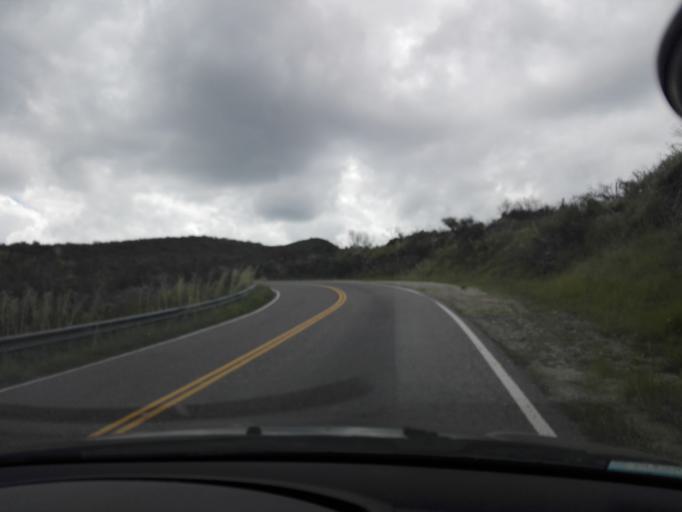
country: AR
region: Cordoba
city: Alta Gracia
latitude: -31.5911
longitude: -64.5140
